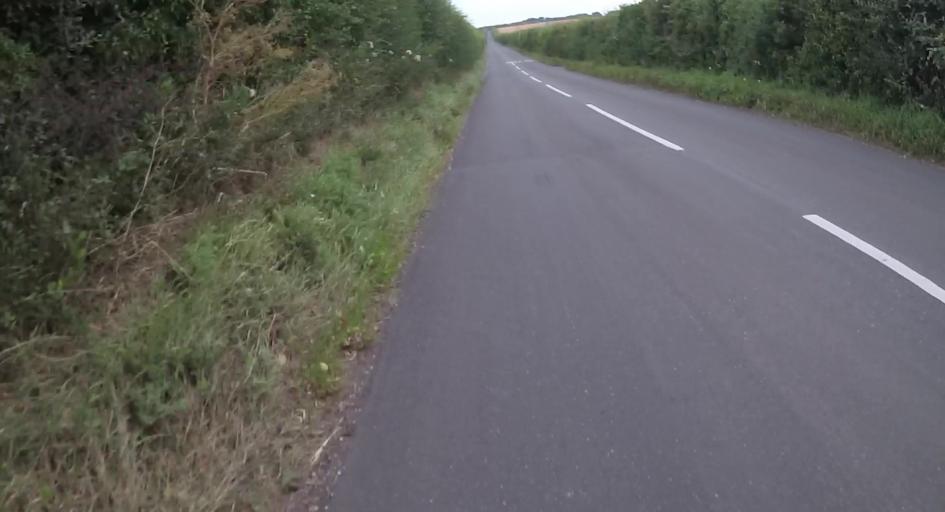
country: GB
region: England
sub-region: Hampshire
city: Kings Worthy
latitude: 51.1375
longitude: -1.3081
